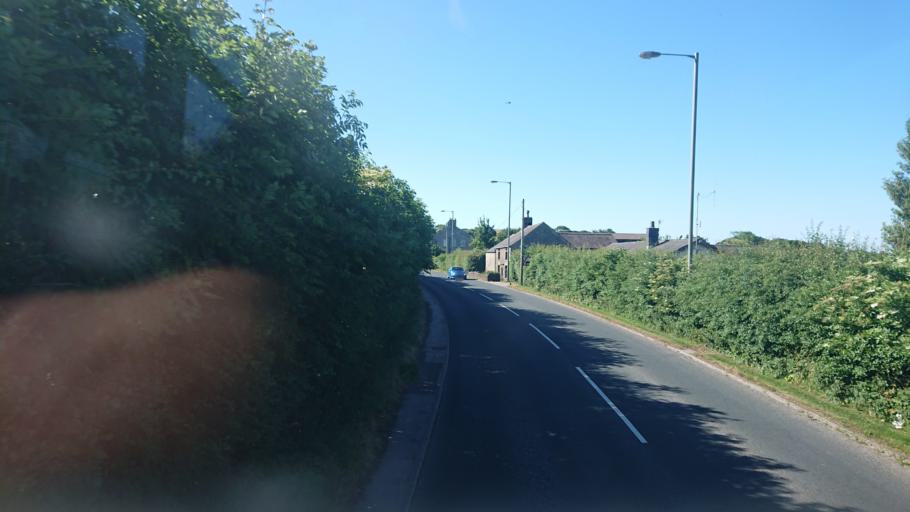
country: GB
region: England
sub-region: Lancashire
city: Galgate
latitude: 53.9878
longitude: -2.7897
